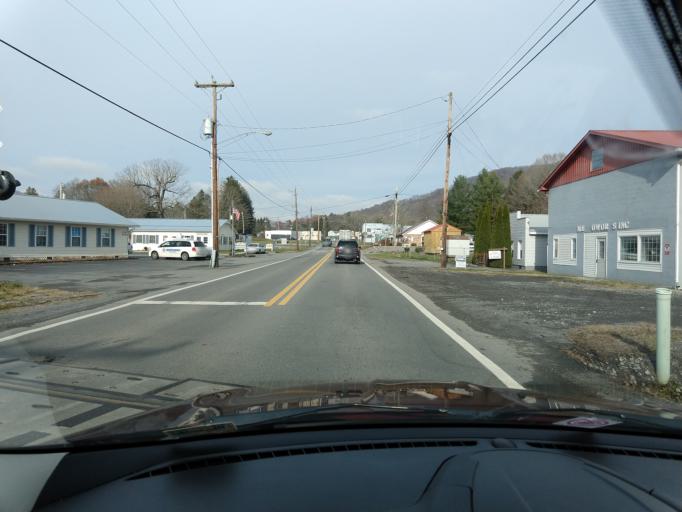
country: US
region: West Virginia
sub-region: Greenbrier County
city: Rainelle
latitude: 37.9609
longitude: -80.6852
